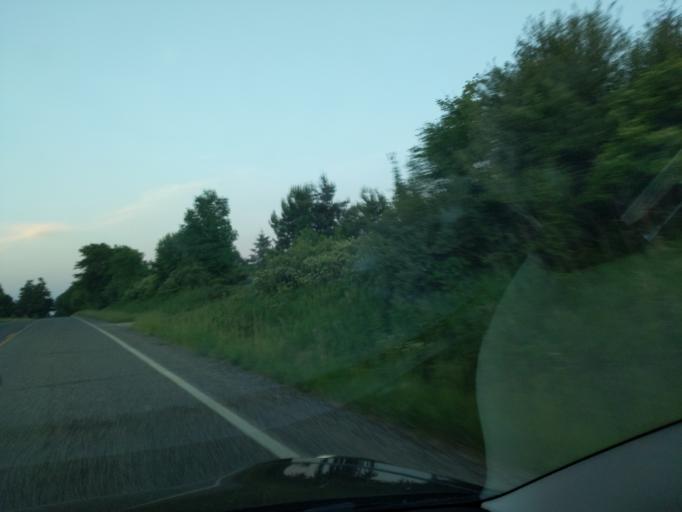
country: US
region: Michigan
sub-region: Barry County
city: Nashville
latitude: 42.5382
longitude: -85.0687
